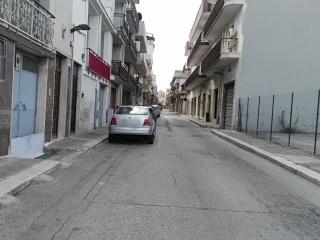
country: IT
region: Apulia
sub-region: Provincia di Bari
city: Triggiano
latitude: 41.0667
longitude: 16.9179
